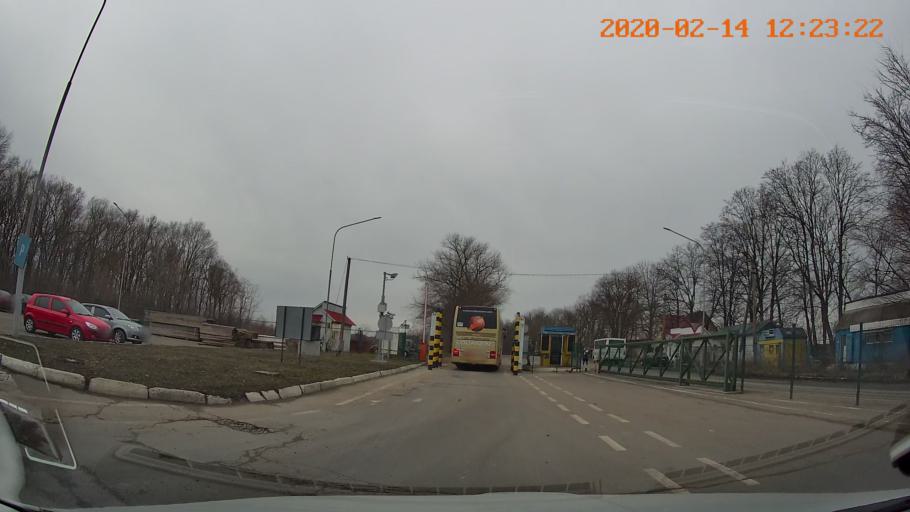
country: RO
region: Botosani
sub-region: Comuna Paltinis
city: Paltinis
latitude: 48.2642
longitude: 26.6204
